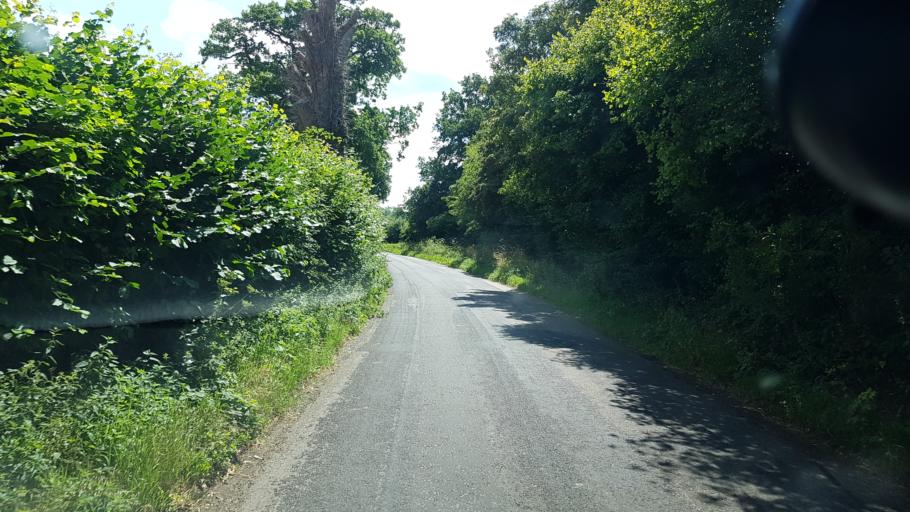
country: GB
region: England
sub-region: Kent
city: Edenbridge
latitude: 51.1977
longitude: 0.1352
